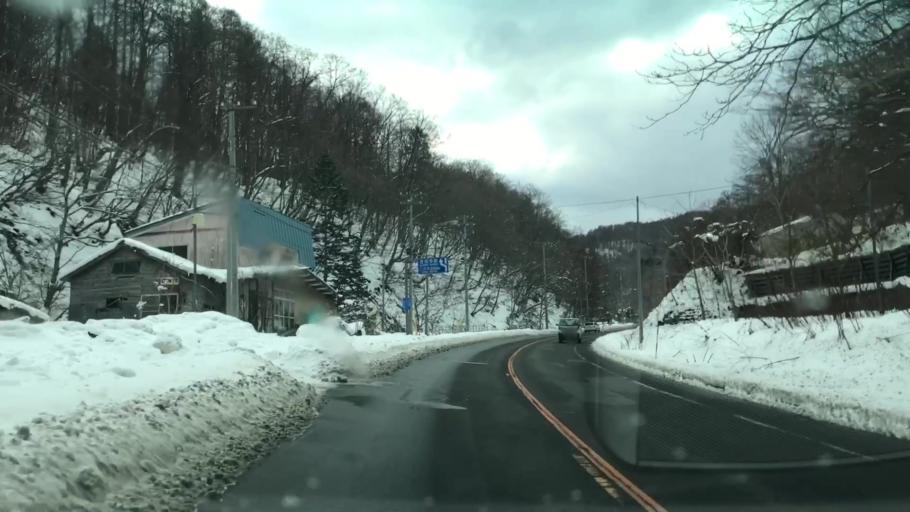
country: JP
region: Hokkaido
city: Yoichi
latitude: 43.2317
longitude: 140.7359
